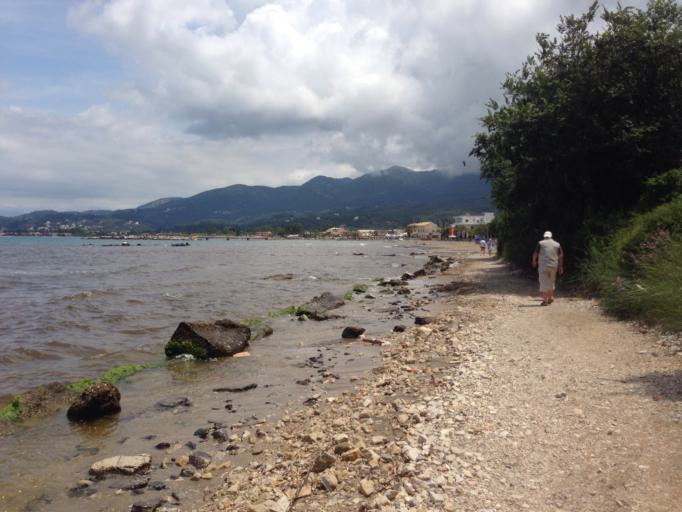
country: GR
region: Ionian Islands
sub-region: Nomos Kerkyras
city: Acharavi
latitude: 39.7926
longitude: 19.7854
